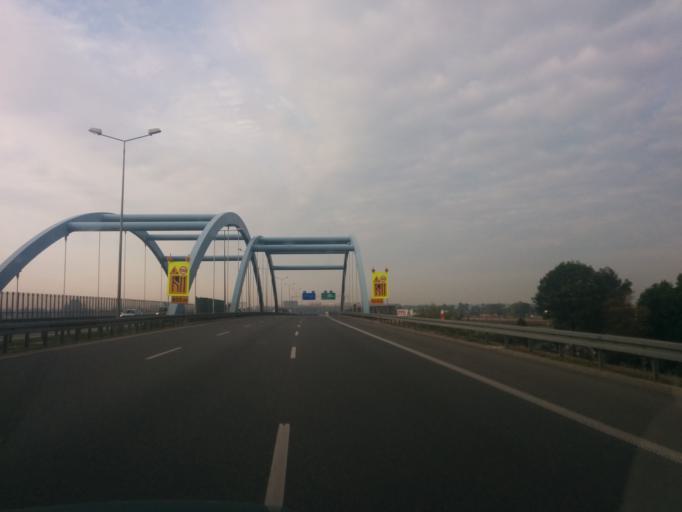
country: PL
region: Masovian Voivodeship
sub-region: Powiat pruszkowski
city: Piastow
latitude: 52.2077
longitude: 20.8533
